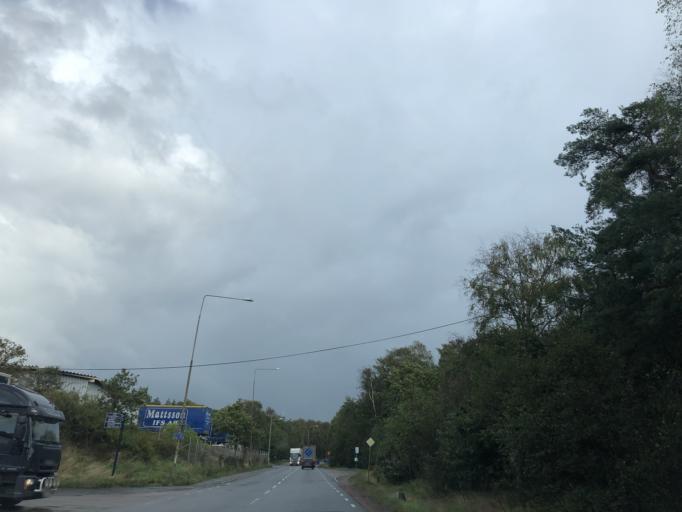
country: SE
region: Vaestra Goetaland
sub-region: Goteborg
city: Torslanda
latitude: 57.7037
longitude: 11.8375
